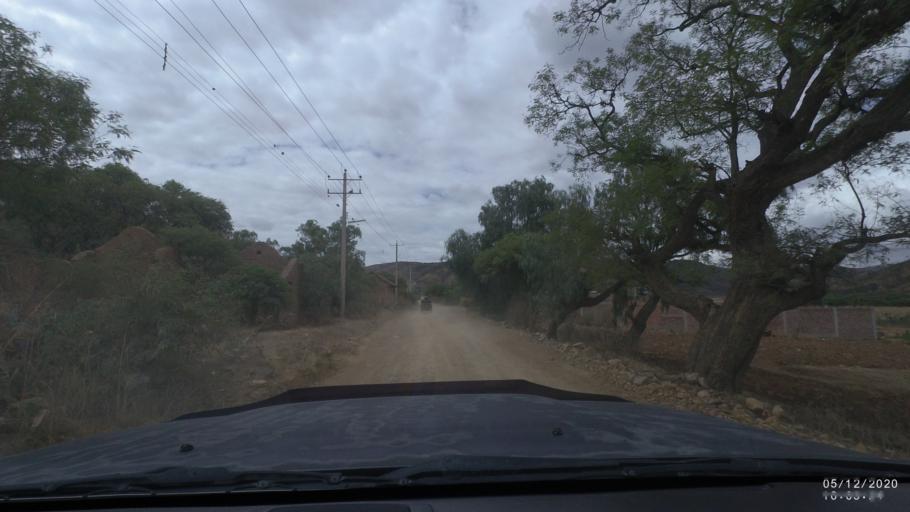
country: BO
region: Cochabamba
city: Sipe Sipe
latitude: -17.4571
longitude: -66.2867
